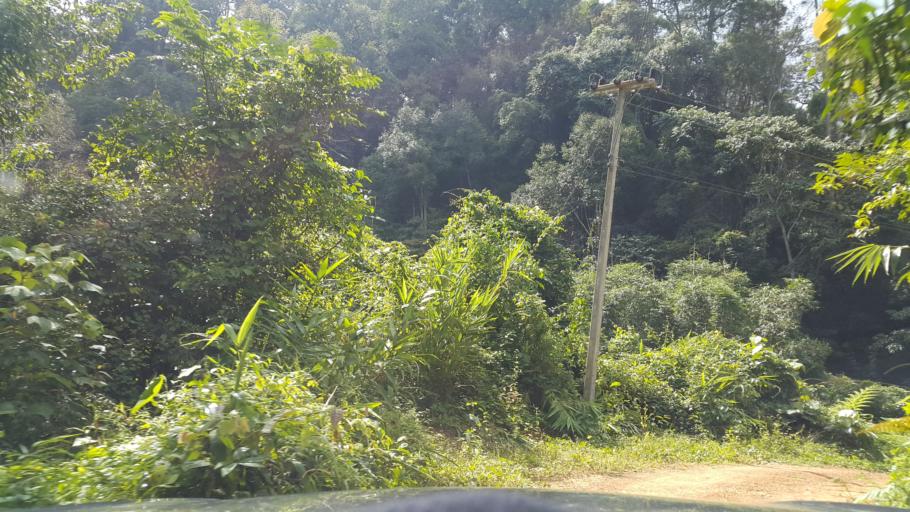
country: TH
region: Chiang Mai
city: Phrao
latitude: 19.1067
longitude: 99.2829
